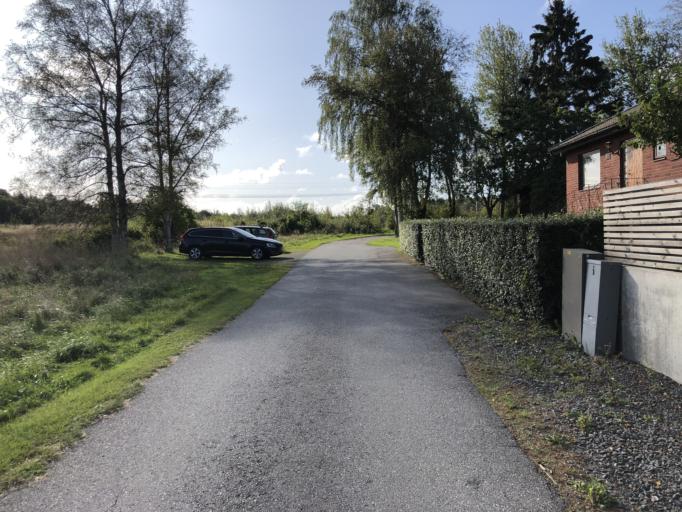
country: SE
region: Vaestra Goetaland
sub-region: Goteborg
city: Torslanda
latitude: 57.7333
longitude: 11.8138
